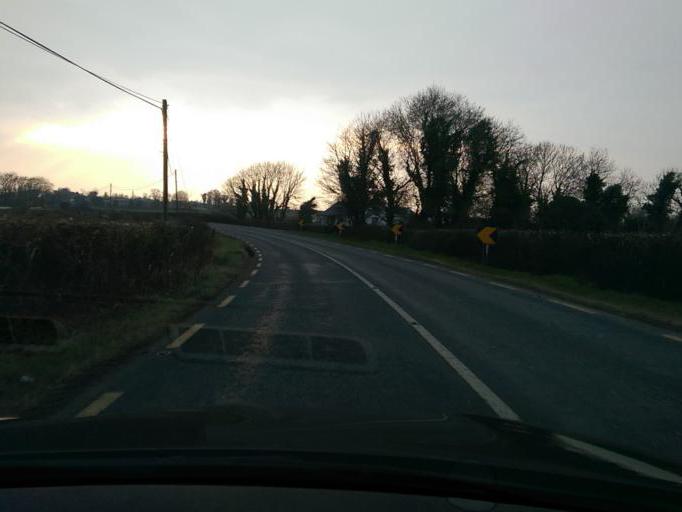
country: IE
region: Leinster
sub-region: An Longfort
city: Ballymahon
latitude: 53.5242
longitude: -7.8039
